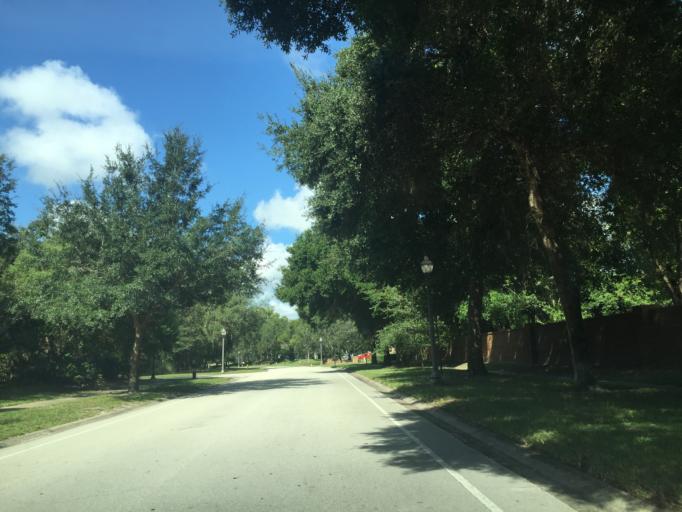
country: US
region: Florida
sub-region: Seminole County
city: Oviedo
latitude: 28.6676
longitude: -81.2384
